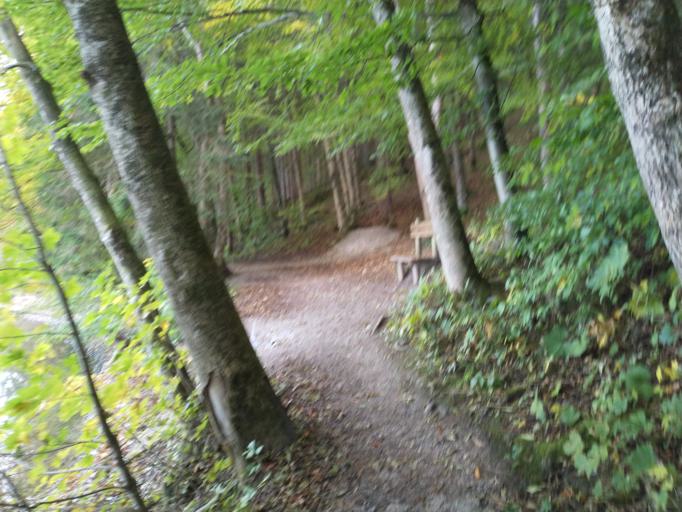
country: AT
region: Tyrol
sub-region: Politischer Bezirk Reutte
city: Vils
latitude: 47.5674
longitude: 10.6391
